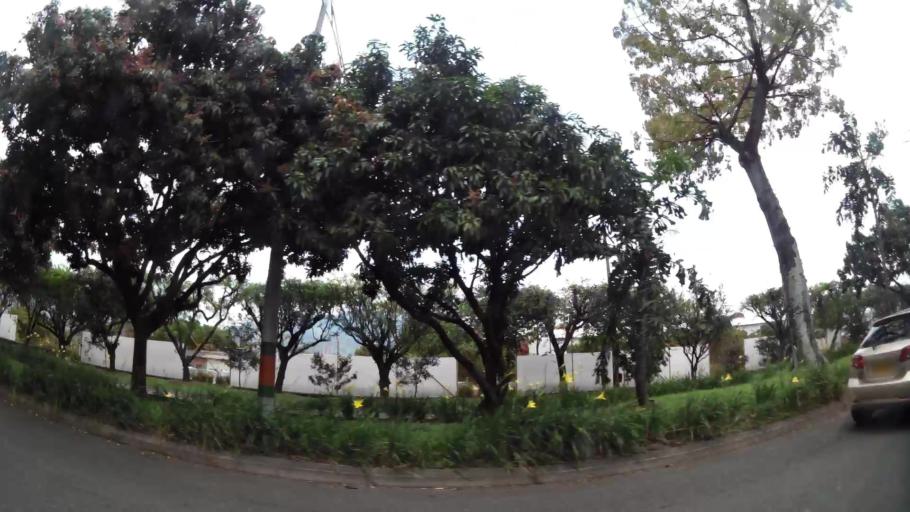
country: CO
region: Antioquia
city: Envigado
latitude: 6.1691
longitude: -75.5966
